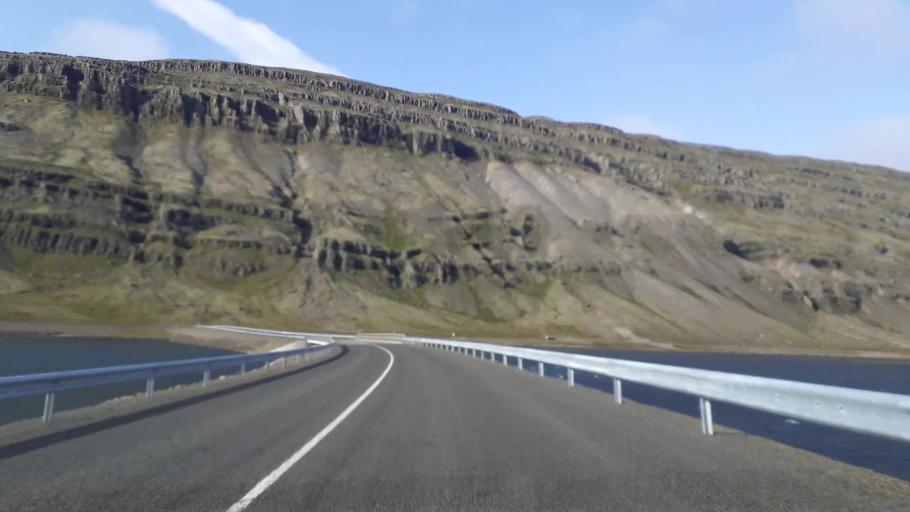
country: IS
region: East
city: Reydarfjoerdur
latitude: 64.7892
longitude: -14.4877
